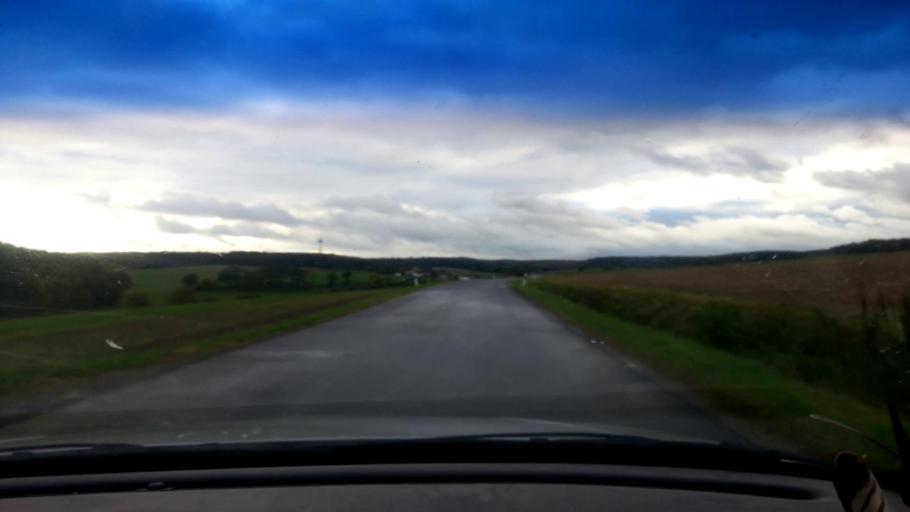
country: DE
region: Bavaria
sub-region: Upper Franconia
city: Burgwindheim
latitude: 49.8104
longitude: 10.6546
